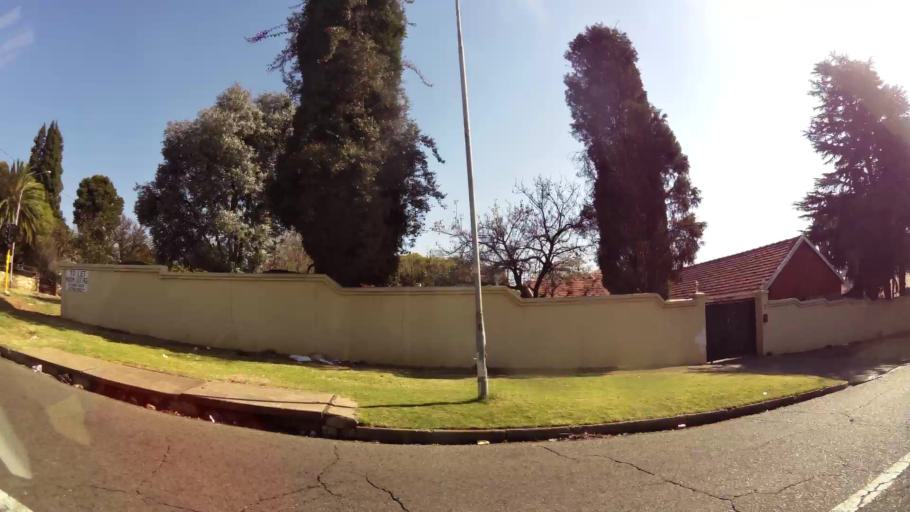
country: ZA
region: Gauteng
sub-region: City of Johannesburg Metropolitan Municipality
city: Johannesburg
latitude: -26.1811
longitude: 28.0751
